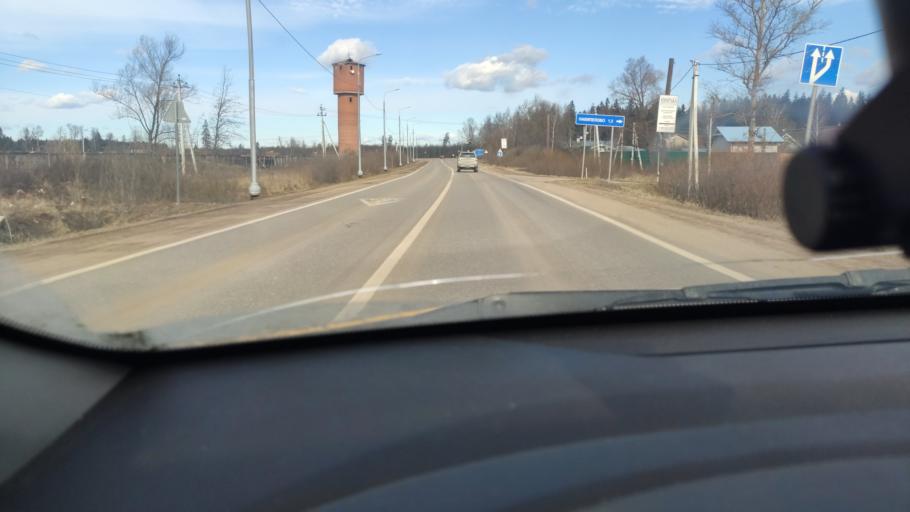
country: RU
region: Moskovskaya
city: Ruza
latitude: 55.7600
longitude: 36.1445
